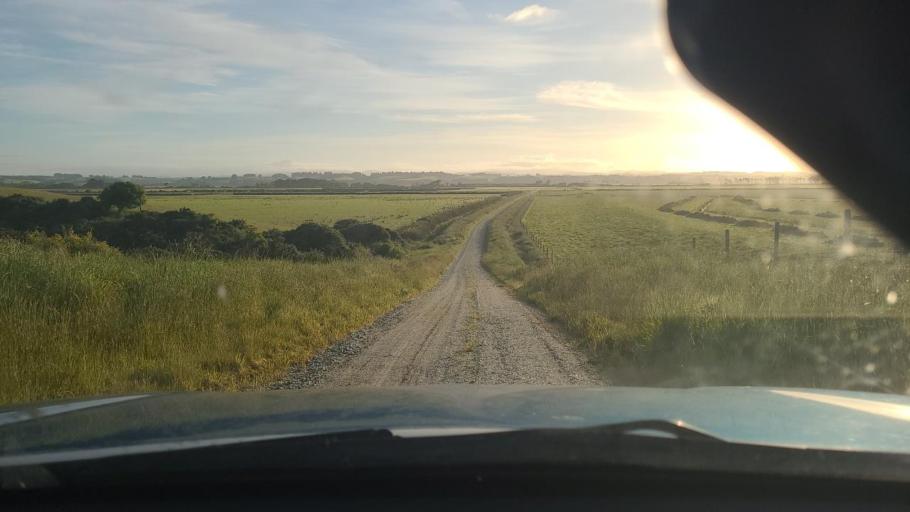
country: NZ
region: Southland
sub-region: Invercargill City
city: Invercargill
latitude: -46.4797
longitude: 168.7195
